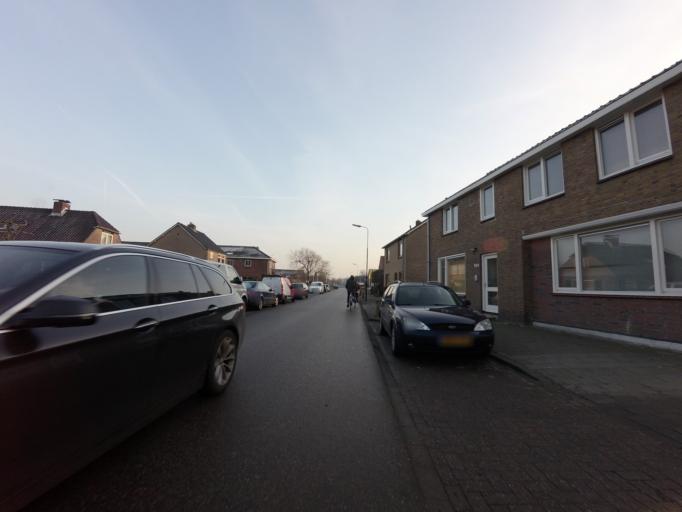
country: NL
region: Utrecht
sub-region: Gemeente De Ronde Venen
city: Mijdrecht
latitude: 52.2228
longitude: 4.9296
